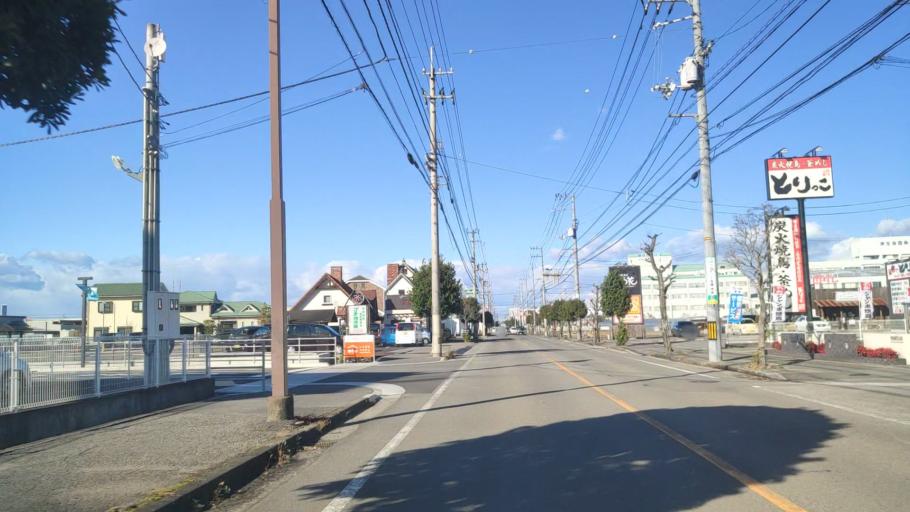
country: JP
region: Ehime
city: Saijo
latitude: 33.9264
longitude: 133.1908
